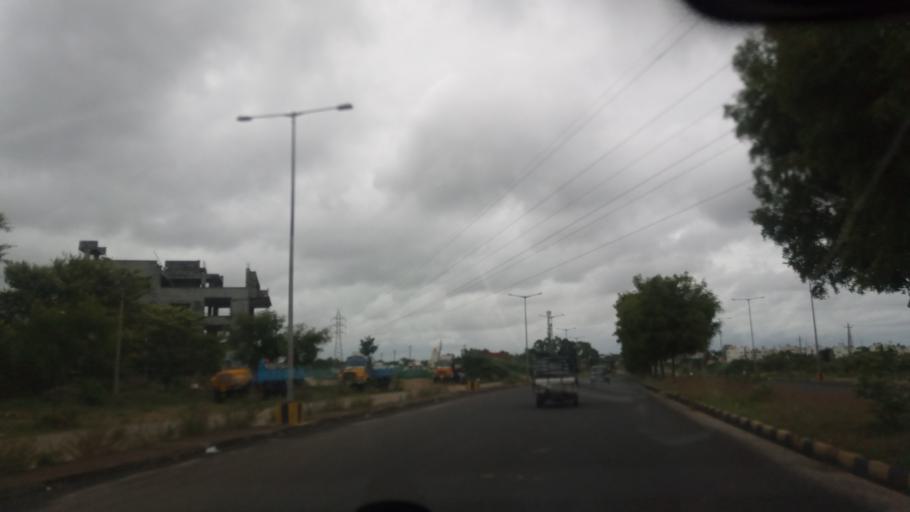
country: IN
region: Karnataka
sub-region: Mysore
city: Mysore
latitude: 12.3152
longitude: 76.5955
